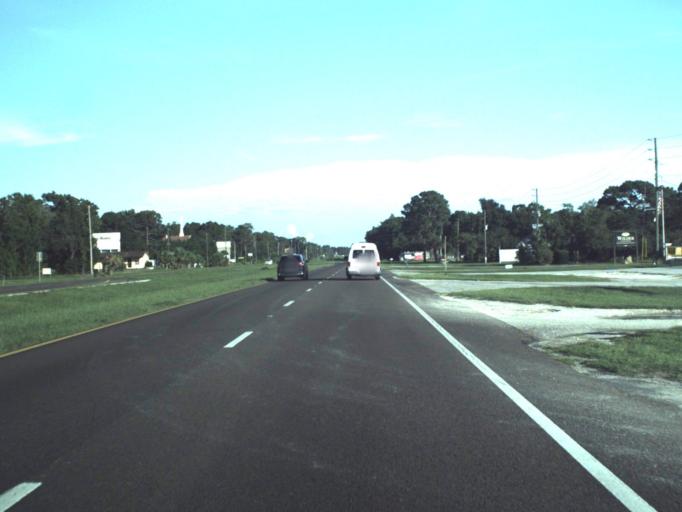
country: US
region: Florida
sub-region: Citrus County
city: Homosassa Springs
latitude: 28.7917
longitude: -82.5697
